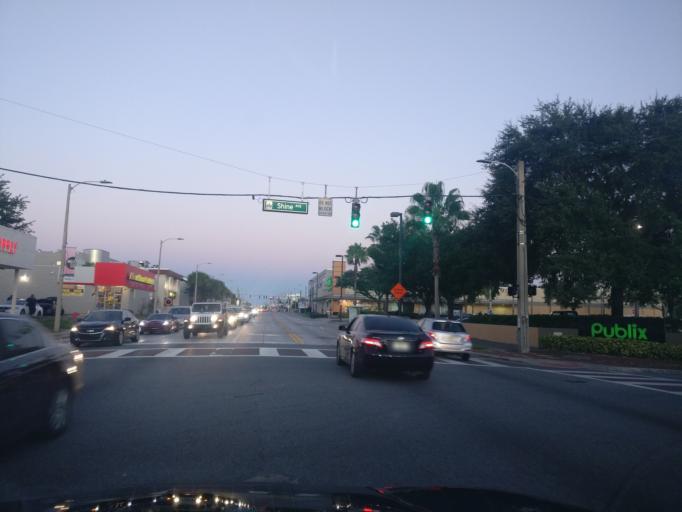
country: US
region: Florida
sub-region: Orange County
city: Orlando
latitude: 28.5531
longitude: -81.3628
